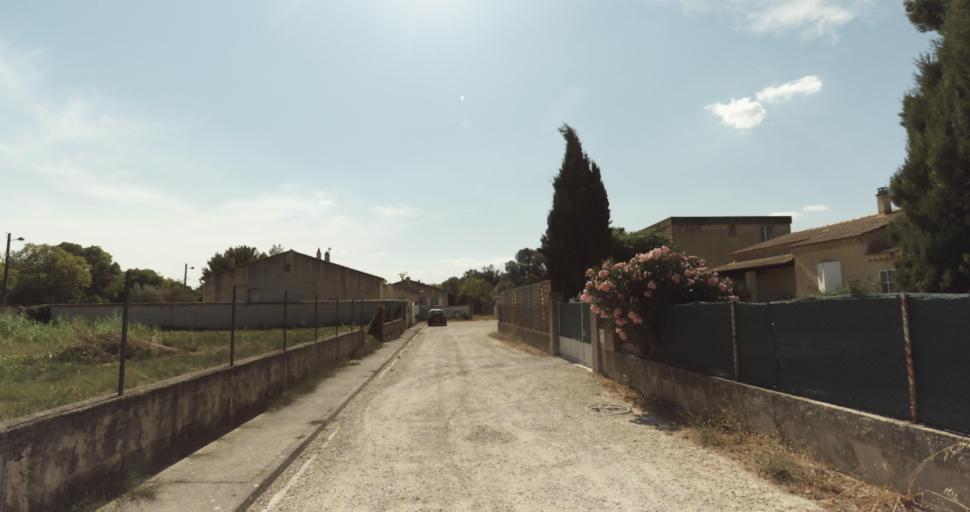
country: FR
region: Provence-Alpes-Cote d'Azur
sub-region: Departement du Vaucluse
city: Monteux
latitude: 44.0385
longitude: 5.0033
